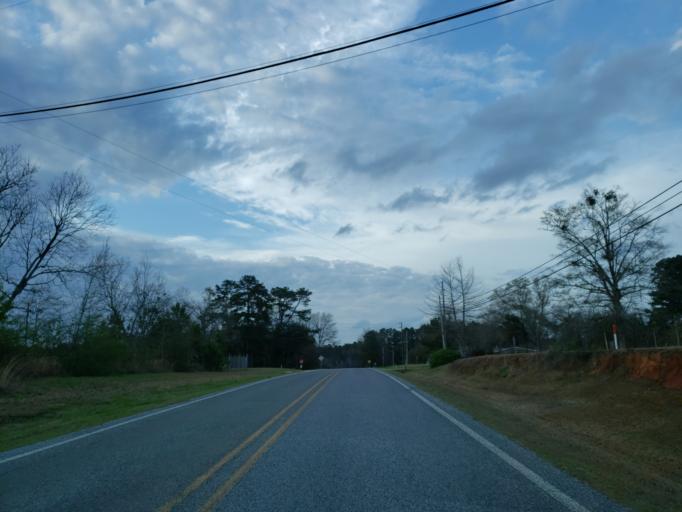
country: US
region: Mississippi
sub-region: Clarke County
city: Stonewall
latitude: 32.2171
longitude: -88.6988
